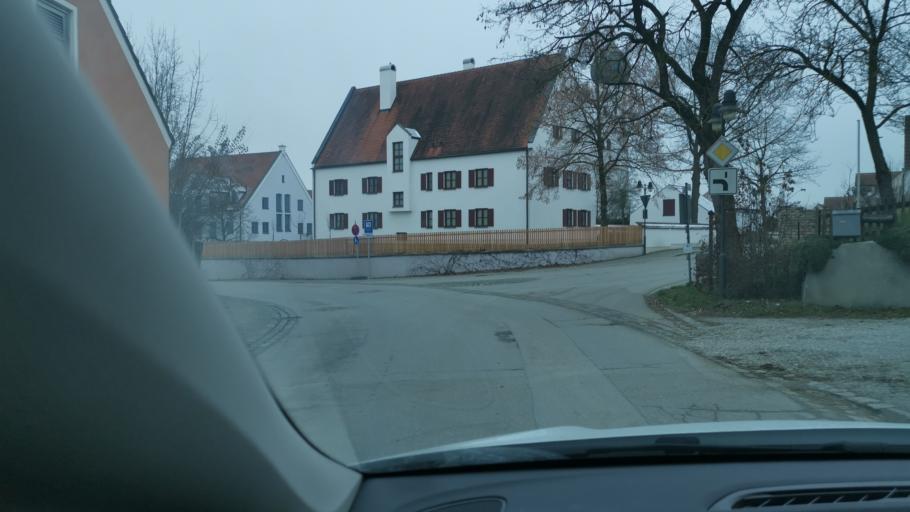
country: DE
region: Bavaria
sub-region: Swabia
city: Rehling
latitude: 48.4871
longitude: 10.9335
